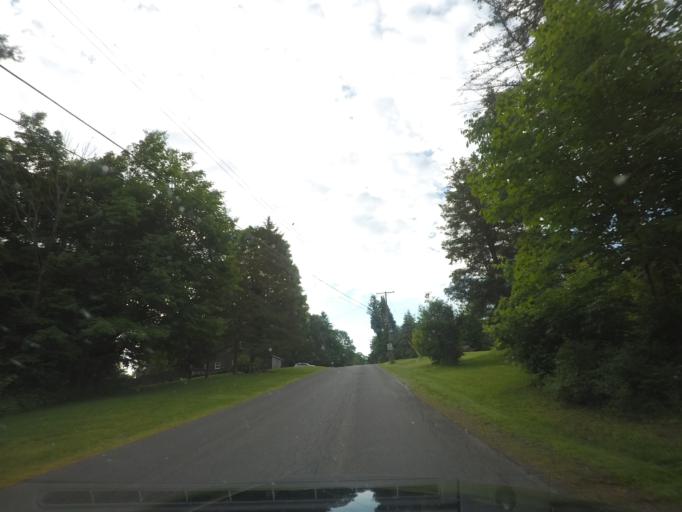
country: US
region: New York
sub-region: Dutchess County
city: Pine Plains
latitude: 41.9638
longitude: -73.5188
